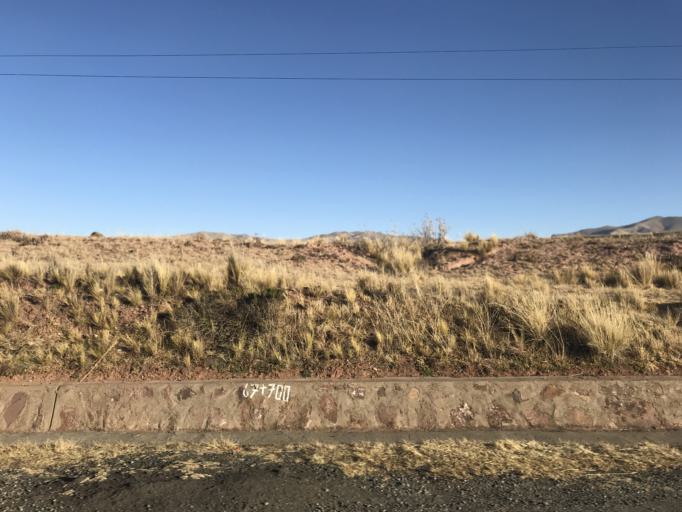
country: BO
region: La Paz
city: Tiahuanaco
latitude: -16.5655
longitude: -68.6410
